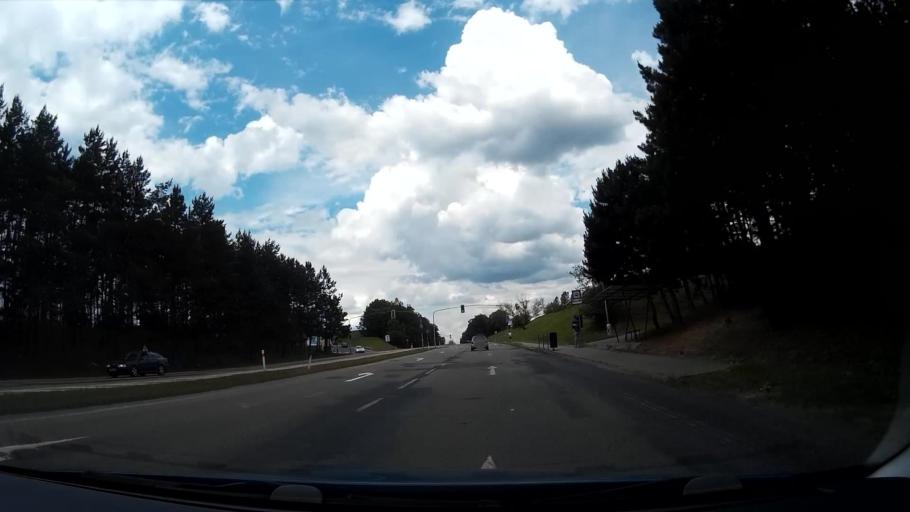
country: CZ
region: South Moravian
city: Troubsko
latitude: 49.2148
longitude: 16.5219
